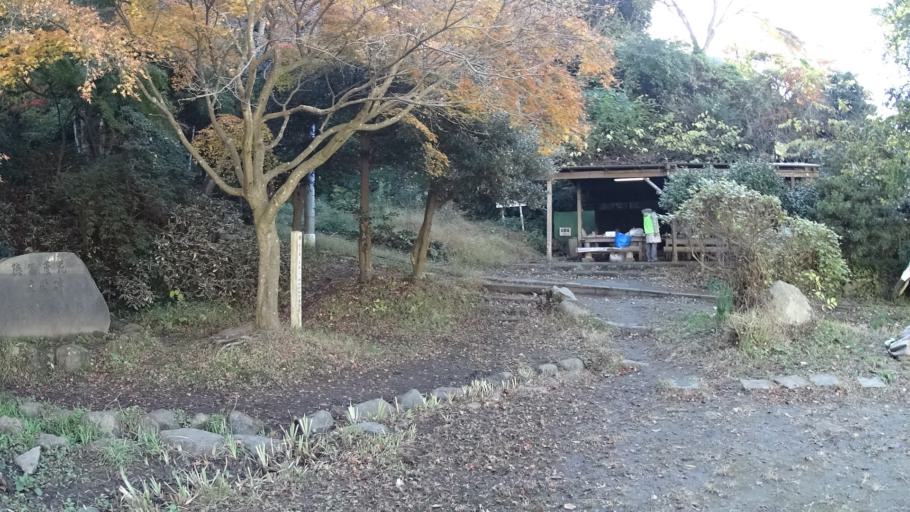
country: JP
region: Kanagawa
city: Zushi
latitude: 35.2870
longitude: 139.5770
